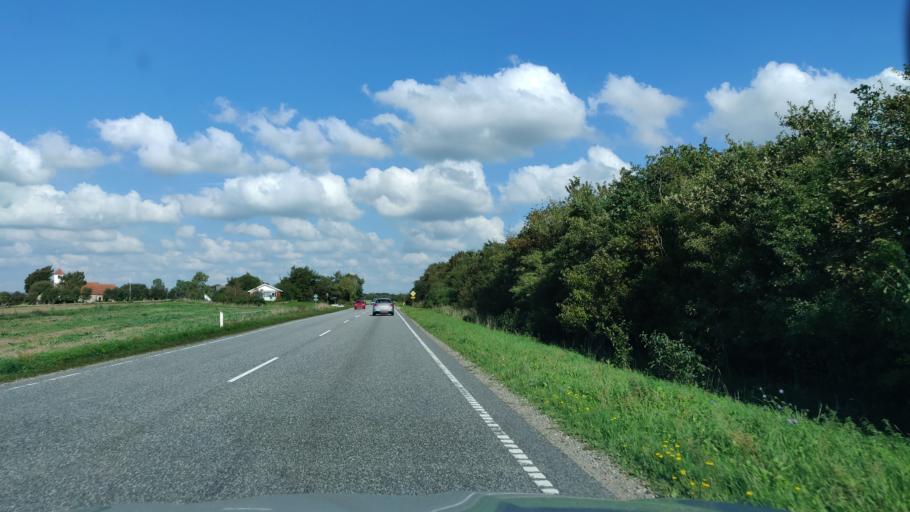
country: DK
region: North Denmark
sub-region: Vesthimmerland Kommune
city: Aars
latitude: 56.7613
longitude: 9.5571
